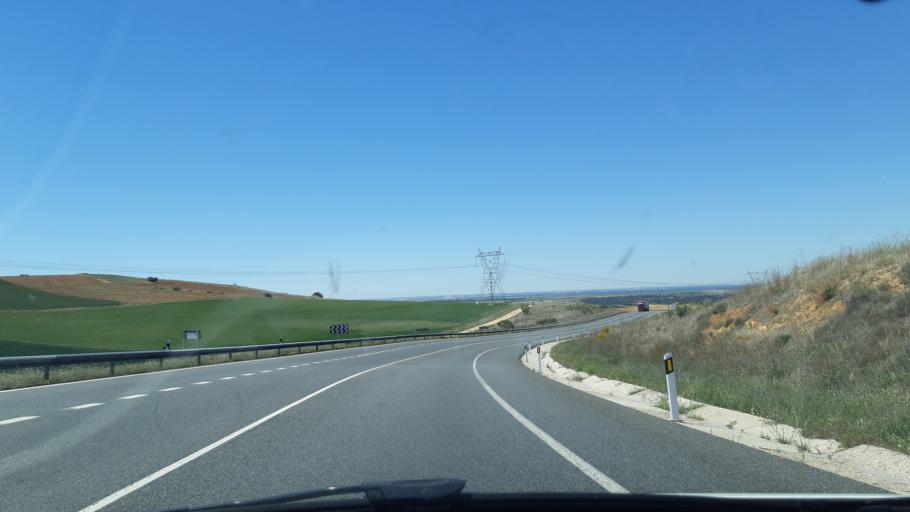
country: ES
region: Castille and Leon
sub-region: Provincia de Segovia
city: Labajos
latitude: 40.8441
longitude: -4.5305
